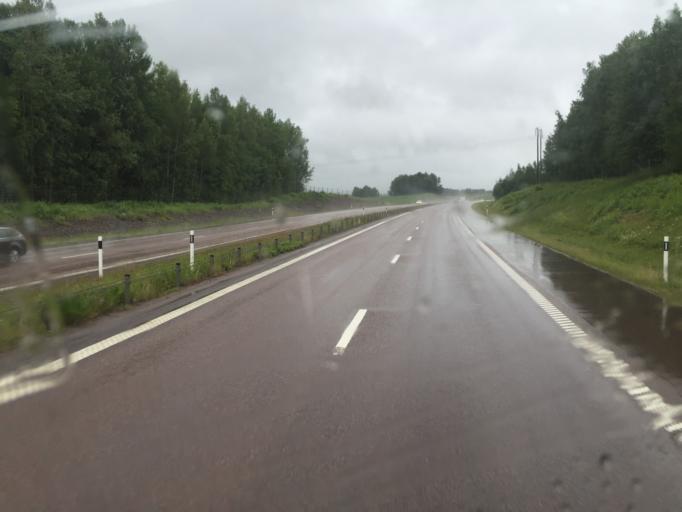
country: SE
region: Dalarna
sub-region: Borlange Kommun
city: Ornas
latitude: 60.4957
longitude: 15.5076
